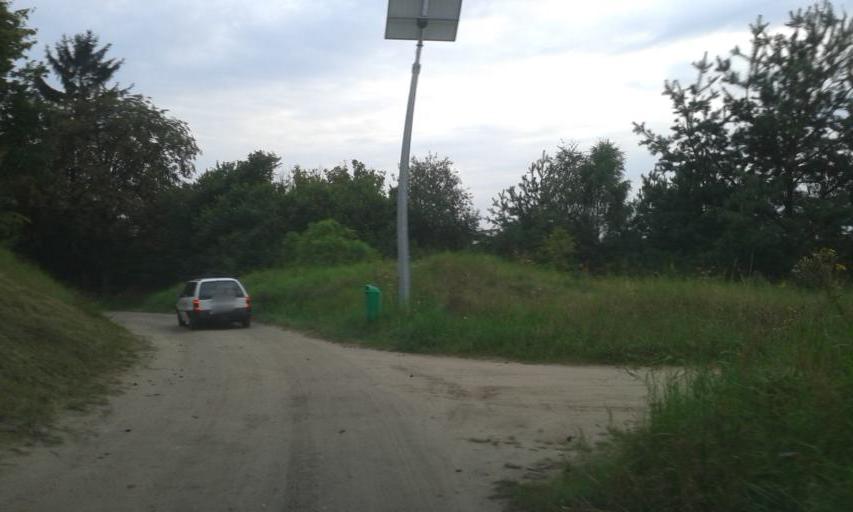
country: PL
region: West Pomeranian Voivodeship
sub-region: Powiat szczecinecki
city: Lubowo
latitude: 53.5887
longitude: 16.3869
